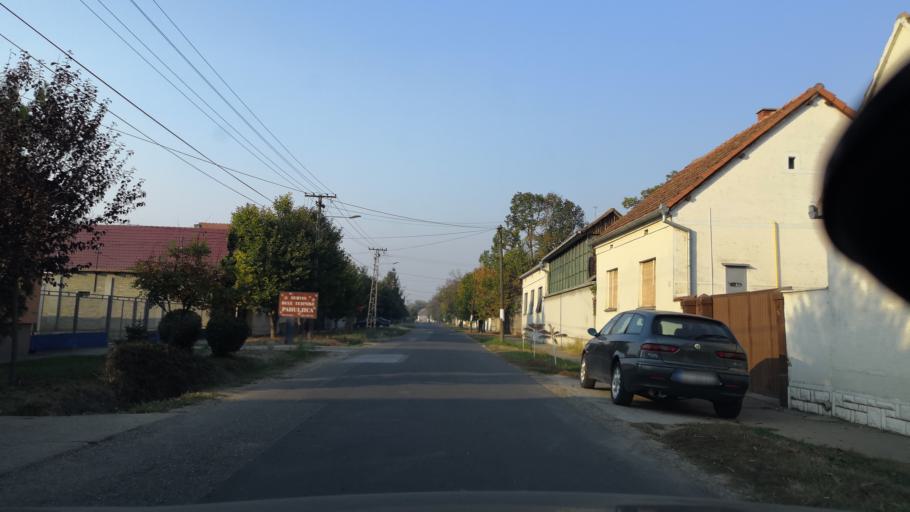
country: RS
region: Autonomna Pokrajina Vojvodina
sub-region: Sremski Okrug
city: Stara Pazova
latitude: 44.9873
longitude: 20.1500
